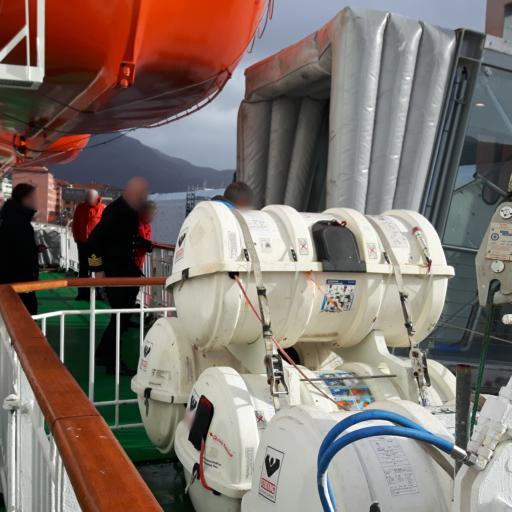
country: NO
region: Hordaland
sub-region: Bergen
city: Bergen
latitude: 60.3924
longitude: 5.3102
